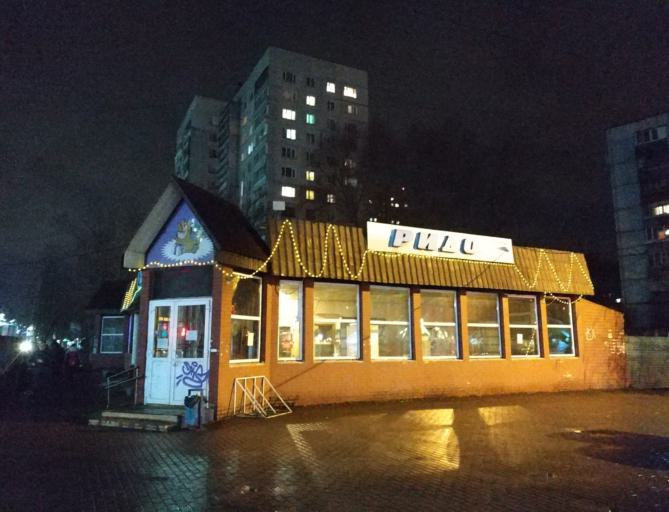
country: RU
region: Moskovskaya
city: Balashikha
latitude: 55.8255
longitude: 37.9713
